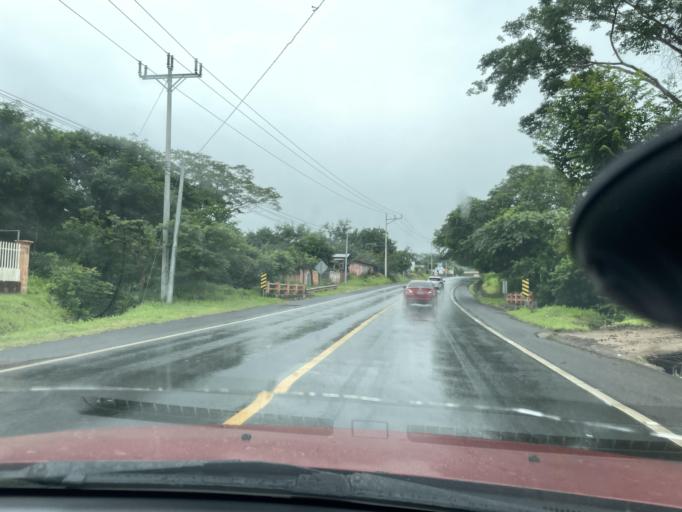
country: SV
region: San Miguel
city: San Miguel
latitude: 13.5438
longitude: -88.1203
